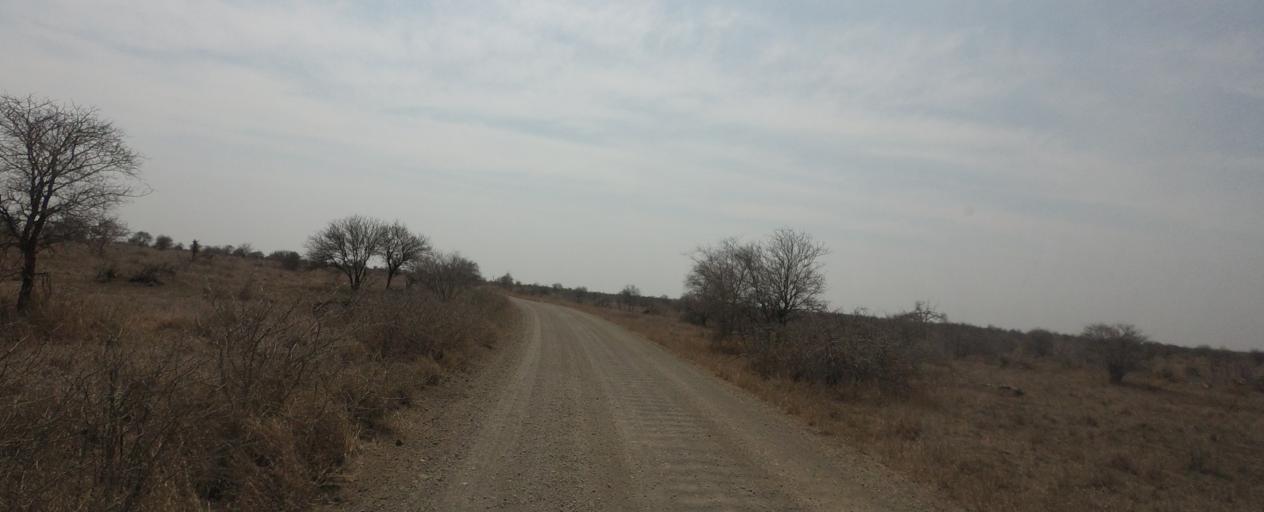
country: ZA
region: Limpopo
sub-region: Mopani District Municipality
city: Phalaborwa
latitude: -24.2614
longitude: 31.6637
